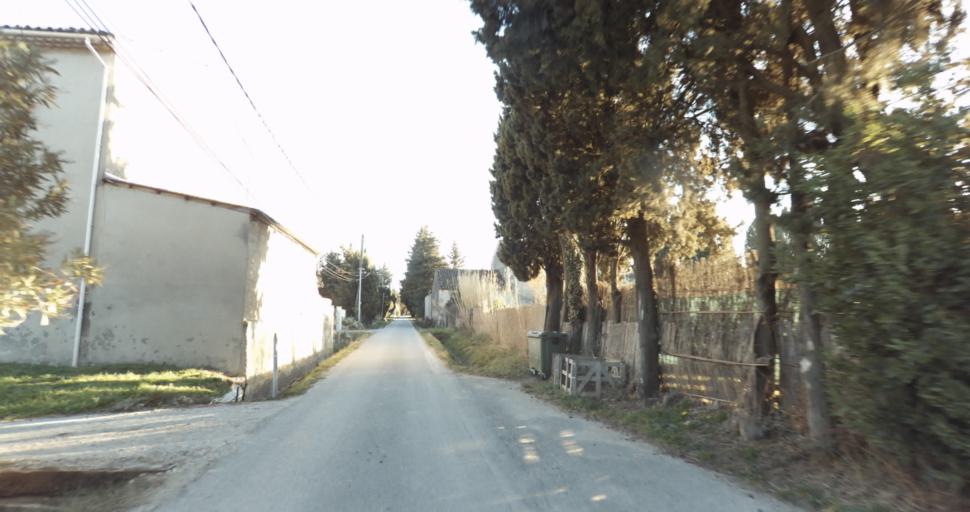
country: FR
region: Provence-Alpes-Cote d'Azur
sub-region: Departement des Bouches-du-Rhone
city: Barbentane
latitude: 43.9111
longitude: 4.7570
